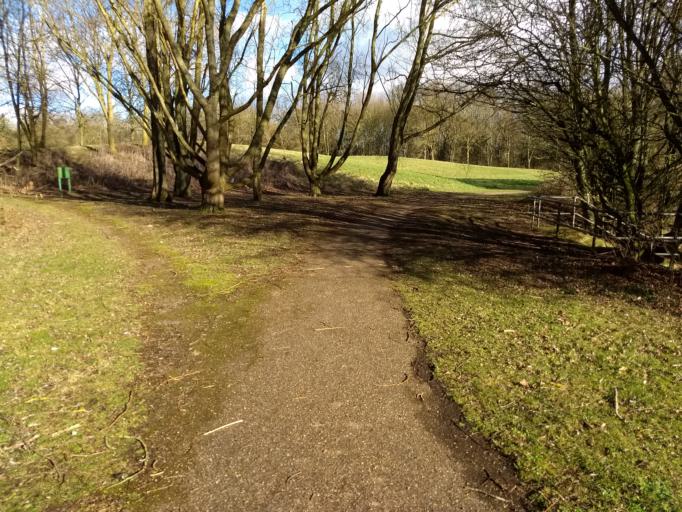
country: GB
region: England
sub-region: Buckinghamshire
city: Bletchley
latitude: 52.0079
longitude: -0.7244
